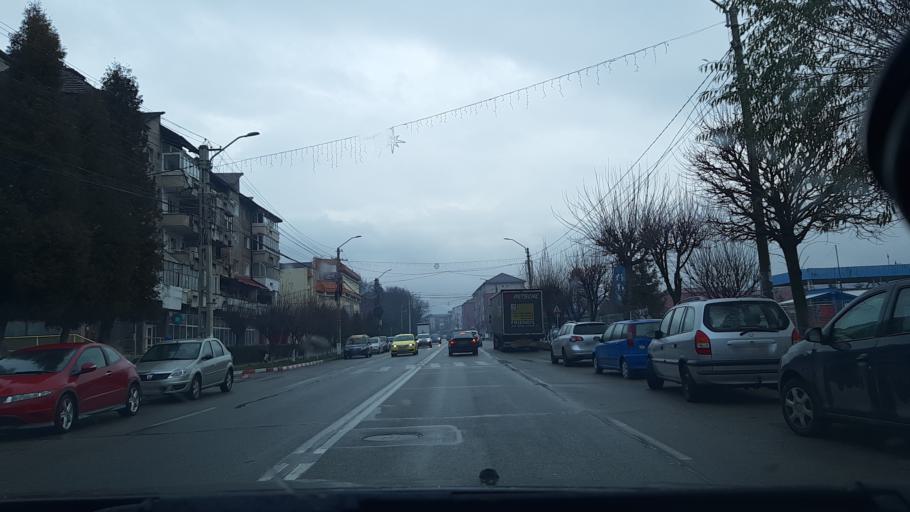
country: RO
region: Hunedoara
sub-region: Municipiul Petrosani
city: Petrosani
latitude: 45.4425
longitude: 23.3745
